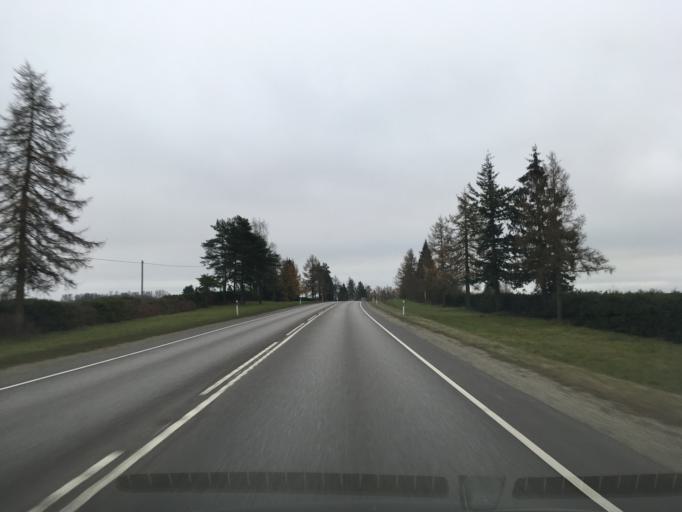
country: EE
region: Laeaene-Virumaa
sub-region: Rakvere linn
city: Rakvere
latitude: 59.4134
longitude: 26.3517
